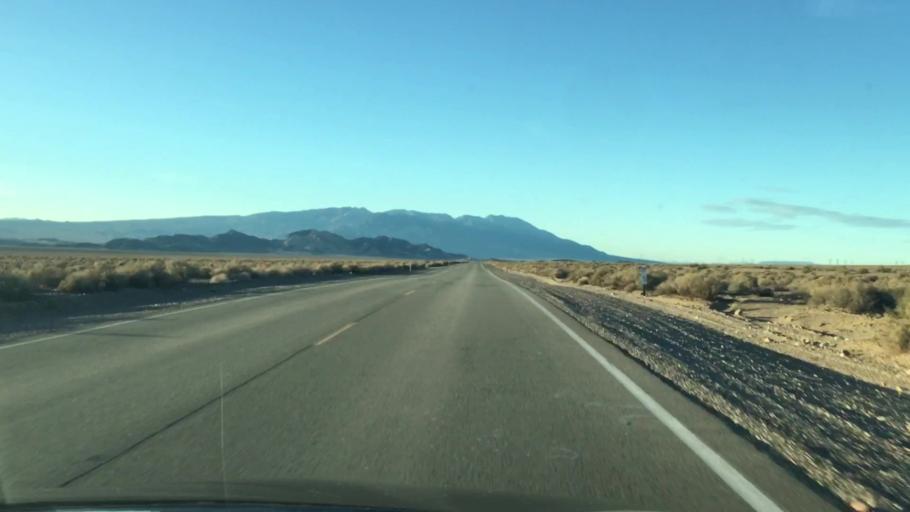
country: US
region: California
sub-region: San Bernardino County
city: Fort Irwin
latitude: 35.3493
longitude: -116.0888
